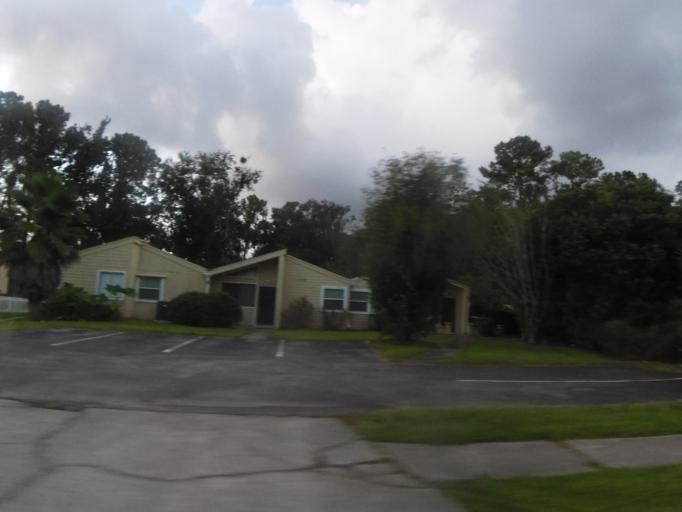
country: US
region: Florida
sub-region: Duval County
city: Jacksonville
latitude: 30.2346
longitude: -81.5999
